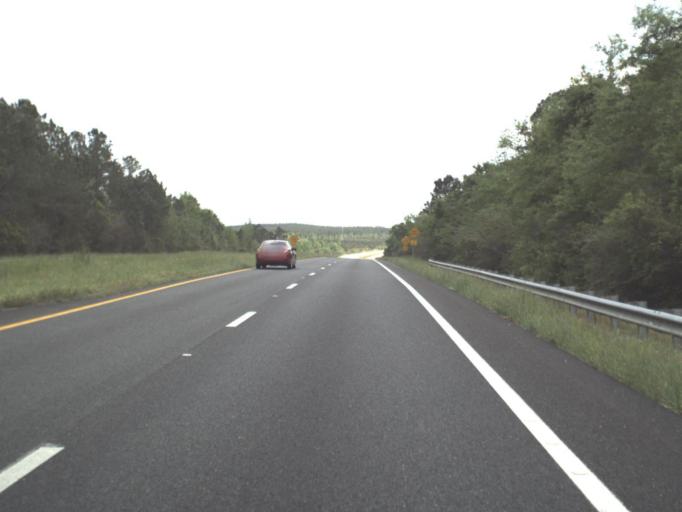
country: US
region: Florida
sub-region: Escambia County
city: Molino
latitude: 30.8016
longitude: -87.3360
